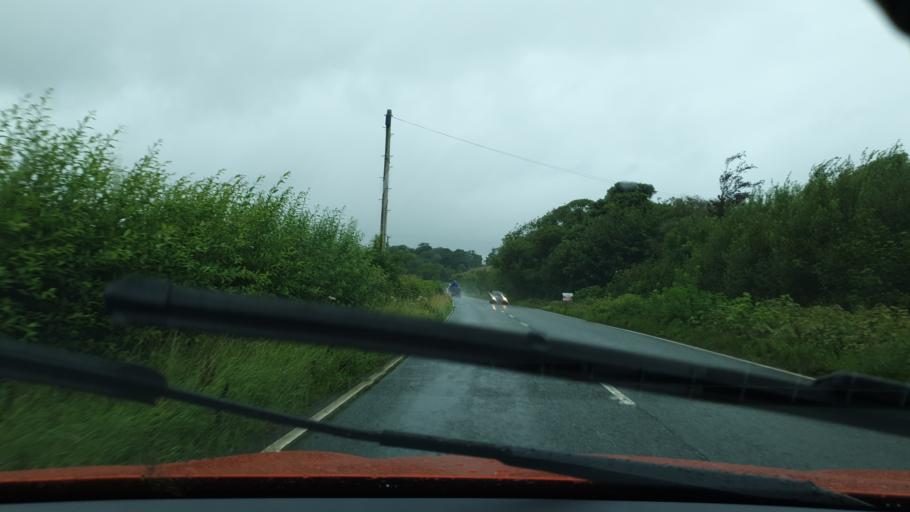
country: GB
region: England
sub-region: Cumbria
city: Askam in Furness
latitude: 54.2677
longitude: -3.1870
